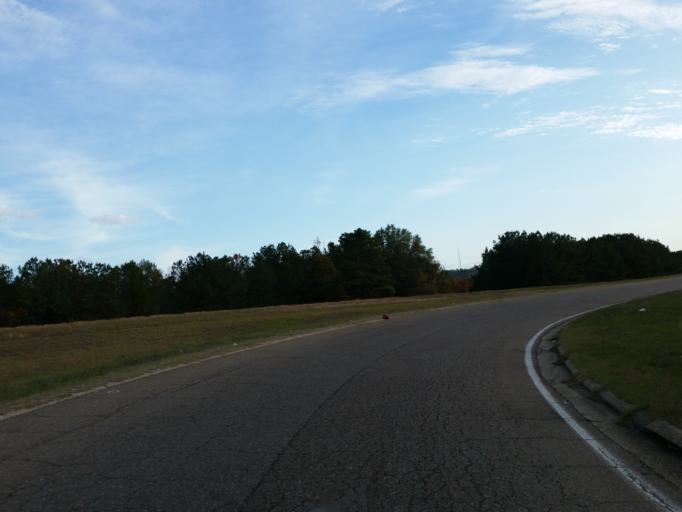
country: US
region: Mississippi
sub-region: Lauderdale County
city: Marion
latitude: 32.3828
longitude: -88.6347
